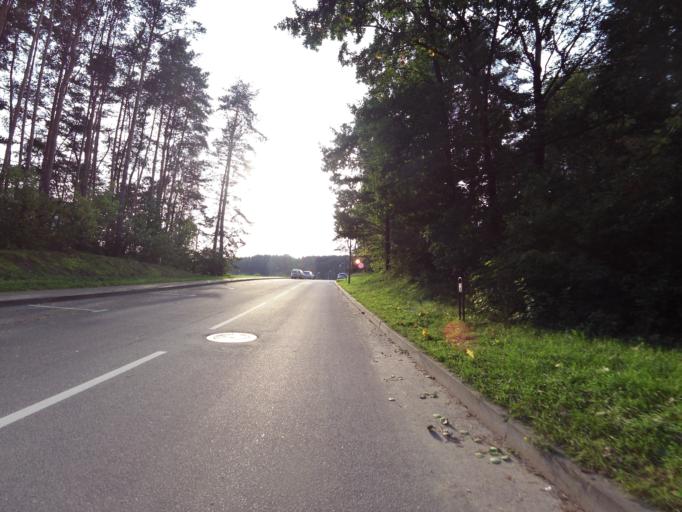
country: LT
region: Vilnius County
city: Lazdynai
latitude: 54.6765
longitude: 25.2257
